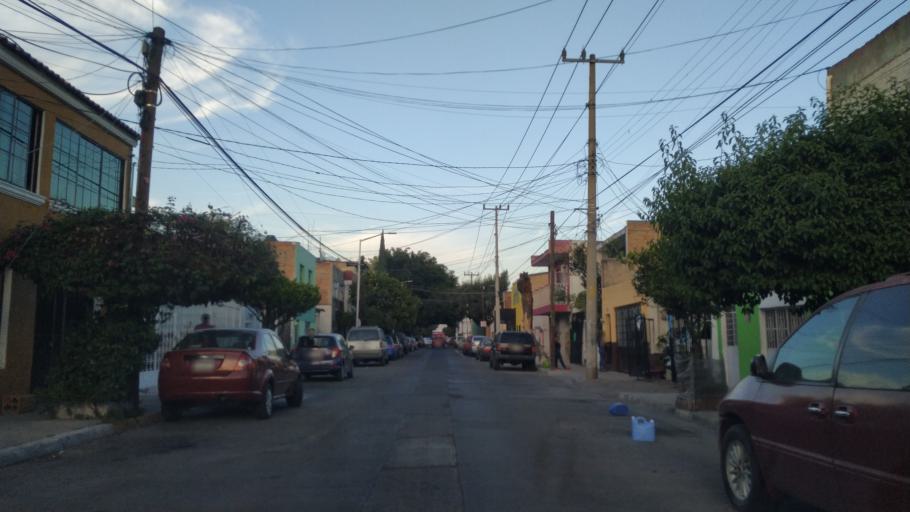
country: MX
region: Jalisco
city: Tlaquepaque
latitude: 20.6508
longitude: -103.3285
